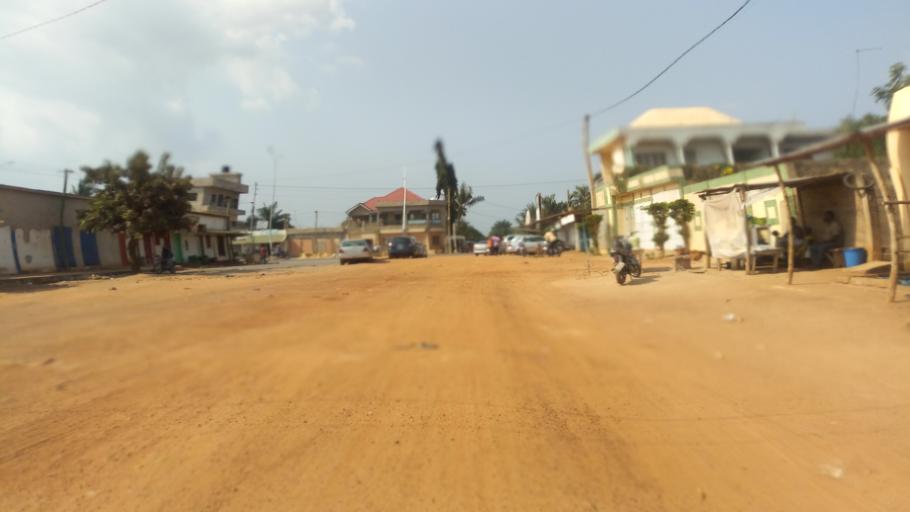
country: TG
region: Maritime
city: Lome
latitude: 6.1980
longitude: 1.1838
